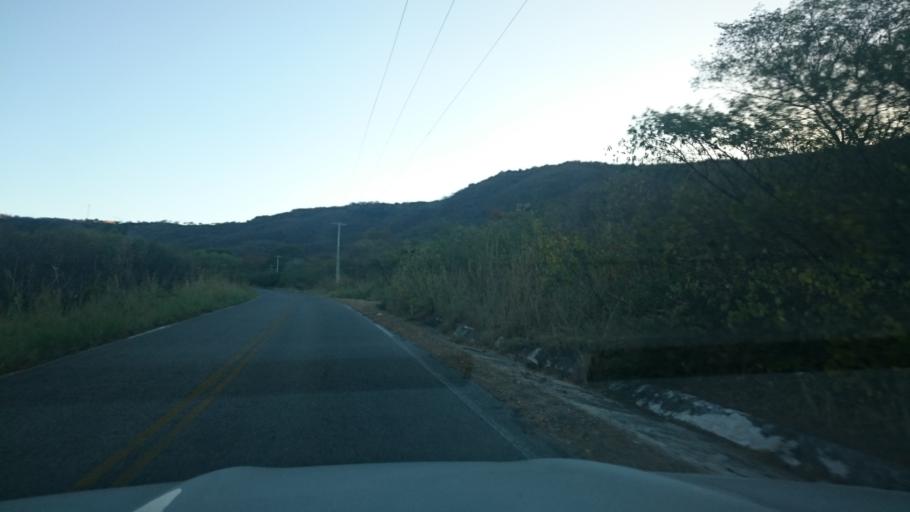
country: BR
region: Rio Grande do Norte
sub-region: Umarizal
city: Umarizal
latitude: -6.0091
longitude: -37.9827
